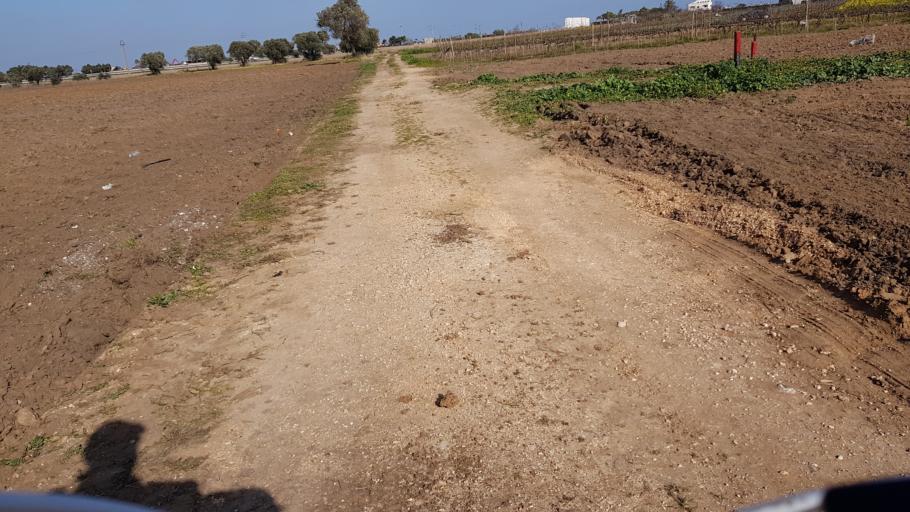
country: IT
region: Apulia
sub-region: Provincia di Brindisi
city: Brindisi
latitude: 40.6093
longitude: 17.8969
